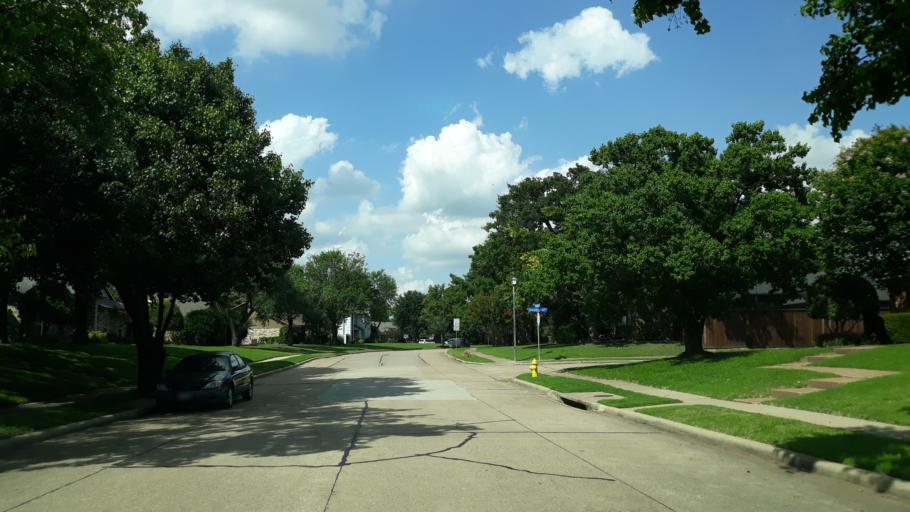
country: US
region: Texas
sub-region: Dallas County
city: Coppell
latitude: 32.9625
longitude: -97.0008
